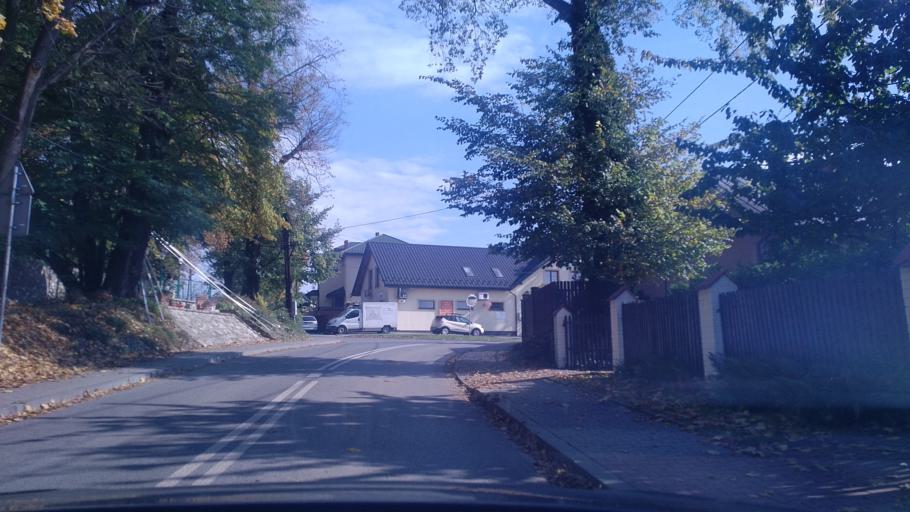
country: PL
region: Lesser Poland Voivodeship
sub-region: Powiat krakowski
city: Modlnica
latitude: 50.1292
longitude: 19.8642
